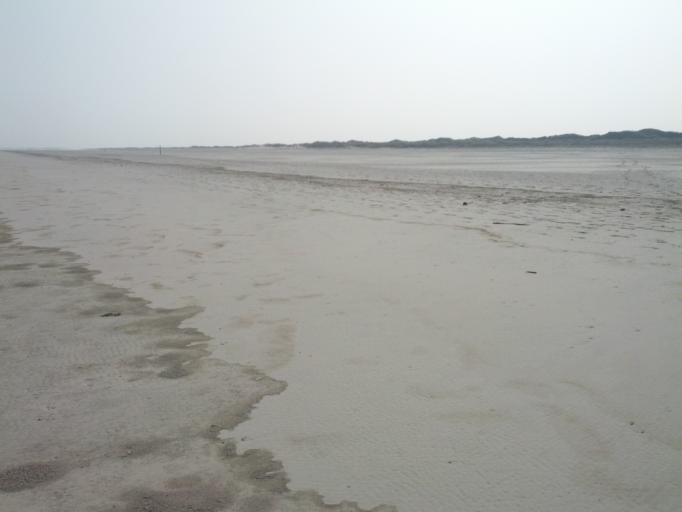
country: DE
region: Lower Saxony
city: Langeoog
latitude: 53.7593
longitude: 7.5884
